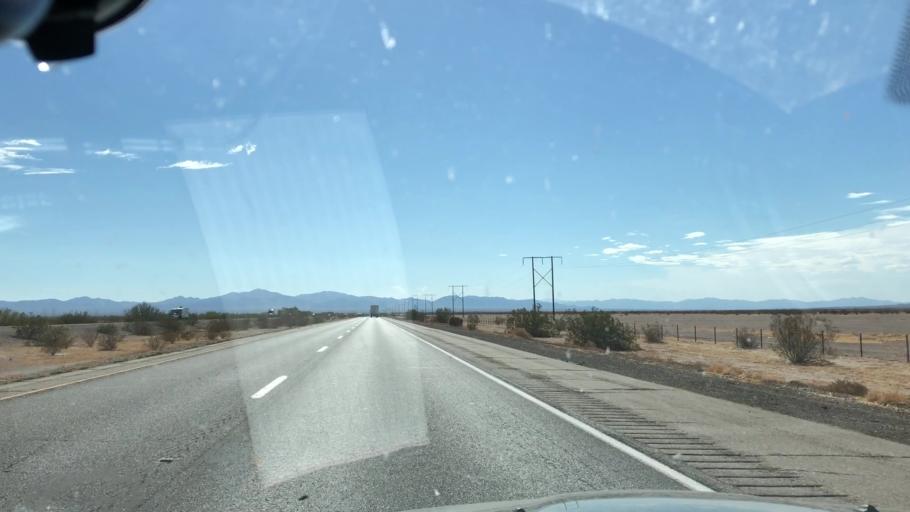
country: US
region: California
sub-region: Riverside County
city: Mesa Verde
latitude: 33.6062
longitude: -114.9339
